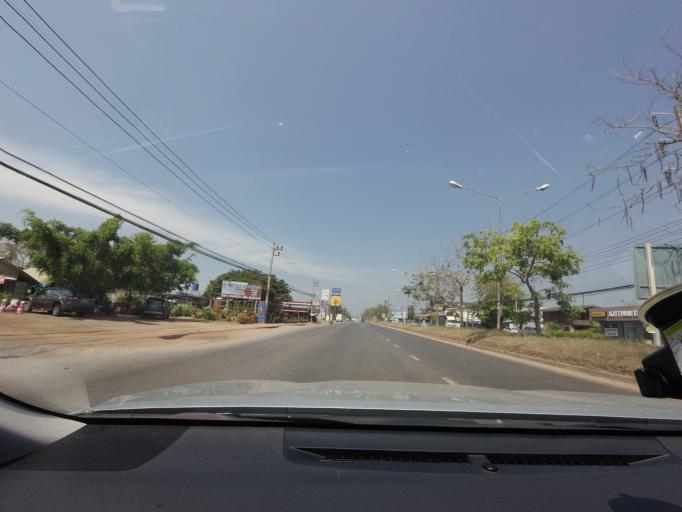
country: TH
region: Surat Thani
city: Surat Thani
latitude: 9.1489
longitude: 99.3804
